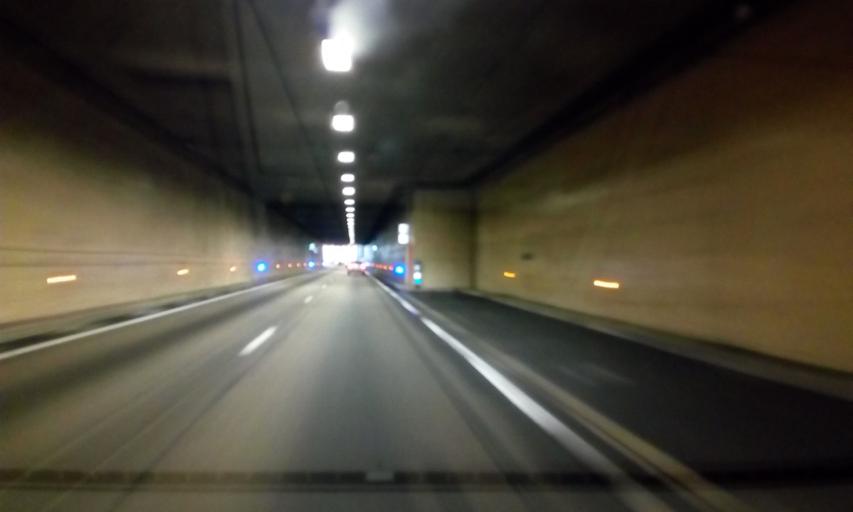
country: FR
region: Provence-Alpes-Cote d'Azur
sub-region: Departement du Var
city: Toulon
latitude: 43.1209
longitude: 5.9461
